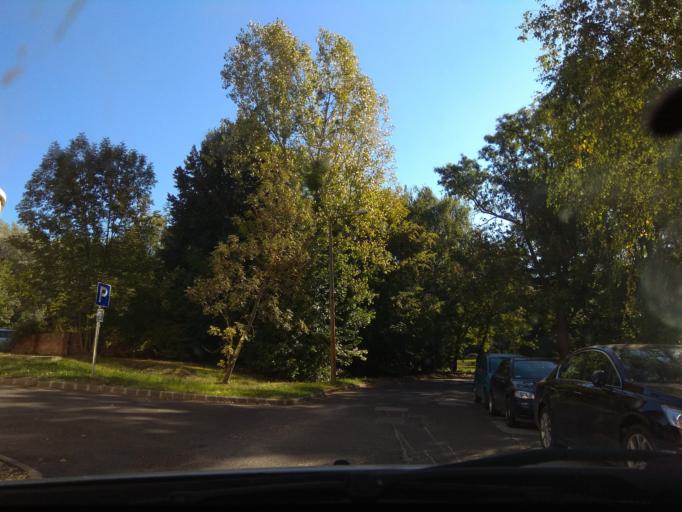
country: HU
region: Borsod-Abauj-Zemplen
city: Miskolc
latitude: 48.0828
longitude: 20.7677
